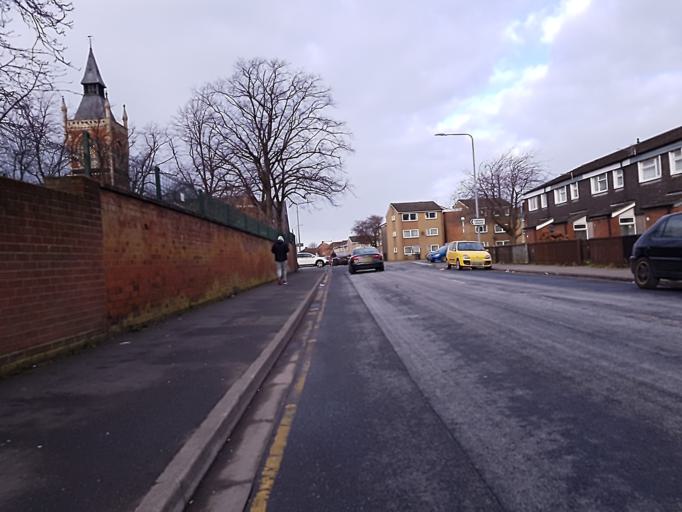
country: GB
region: England
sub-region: North East Lincolnshire
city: Grimsby
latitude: 53.5684
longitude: -0.0704
